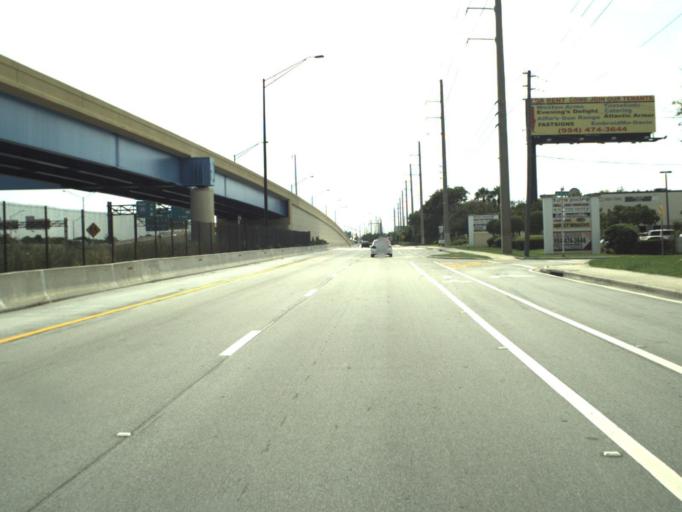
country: US
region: Florida
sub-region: Broward County
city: Pine Island Ridge
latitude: 26.0964
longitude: -80.2417
